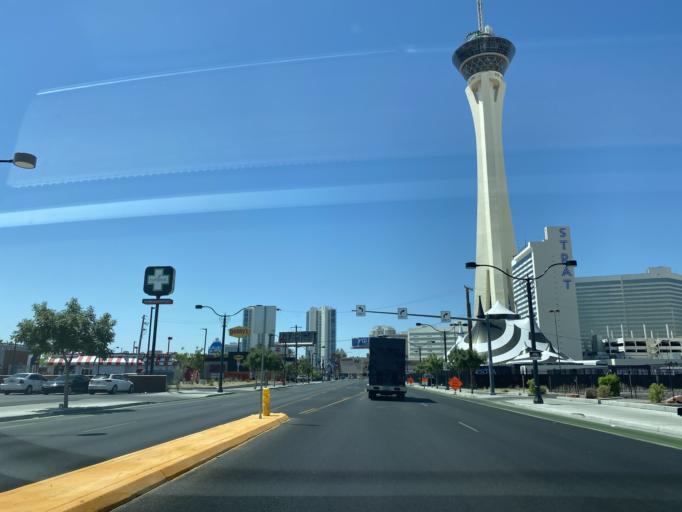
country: US
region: Nevada
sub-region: Clark County
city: Las Vegas
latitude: 36.1509
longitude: -115.1542
